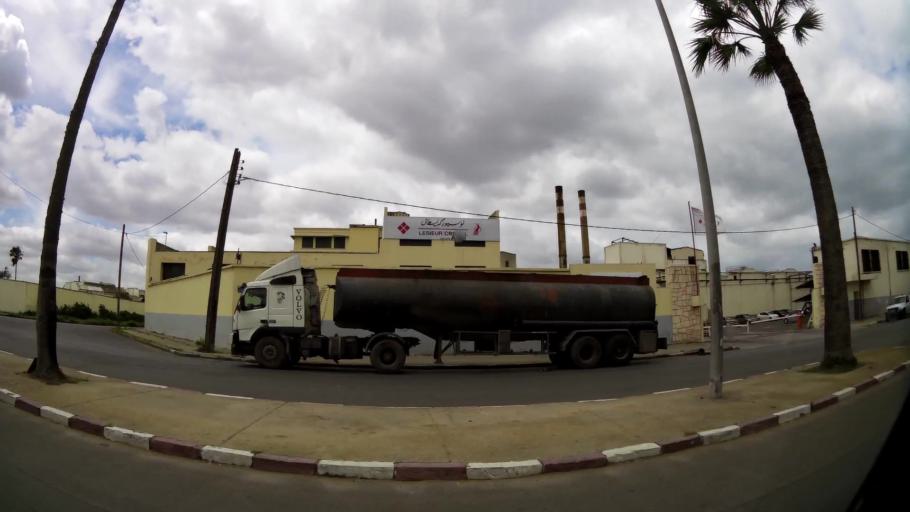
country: MA
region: Grand Casablanca
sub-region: Casablanca
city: Casablanca
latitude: 33.6074
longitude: -7.5639
